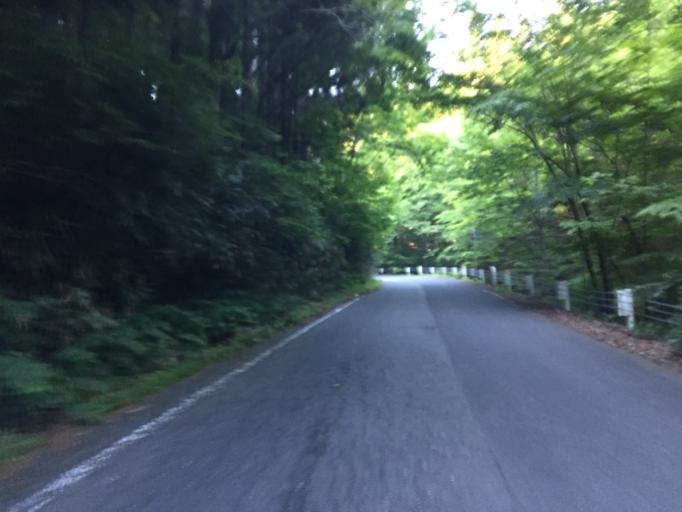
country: JP
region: Ibaraki
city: Kitaibaraki
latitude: 36.8858
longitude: 140.6268
